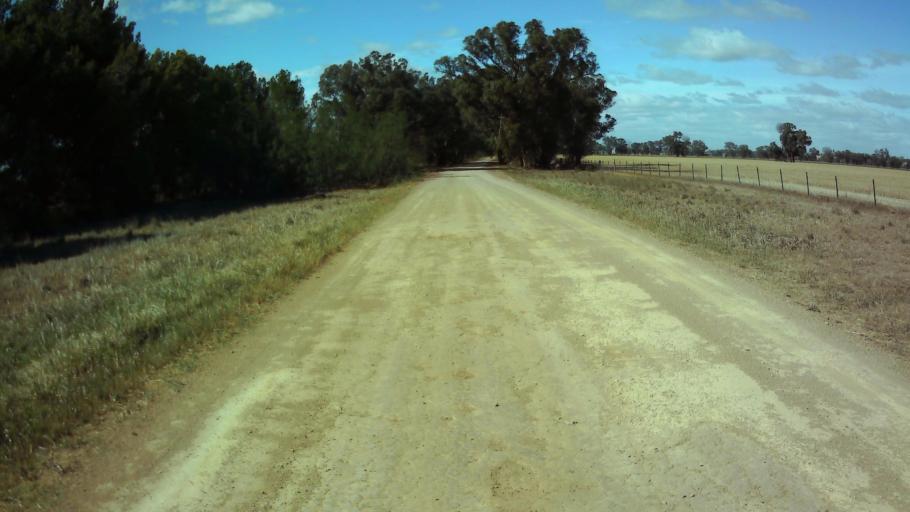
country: AU
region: New South Wales
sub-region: Weddin
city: Grenfell
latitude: -34.0354
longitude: 148.3167
